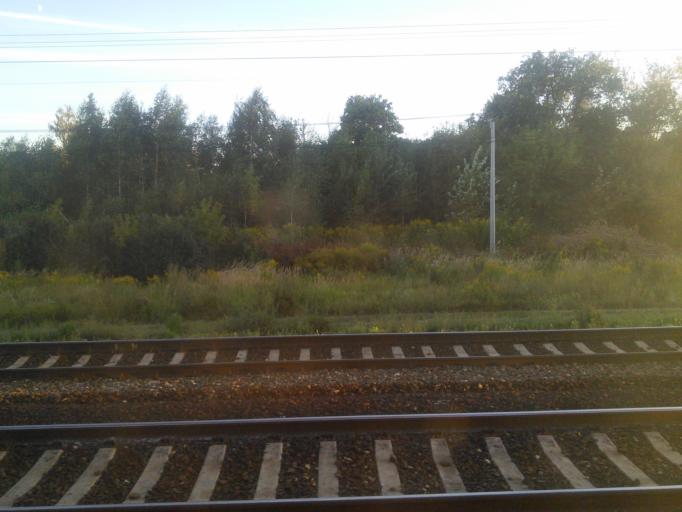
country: RU
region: Moskovskaya
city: Kupavna
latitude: 55.7507
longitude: 38.1311
